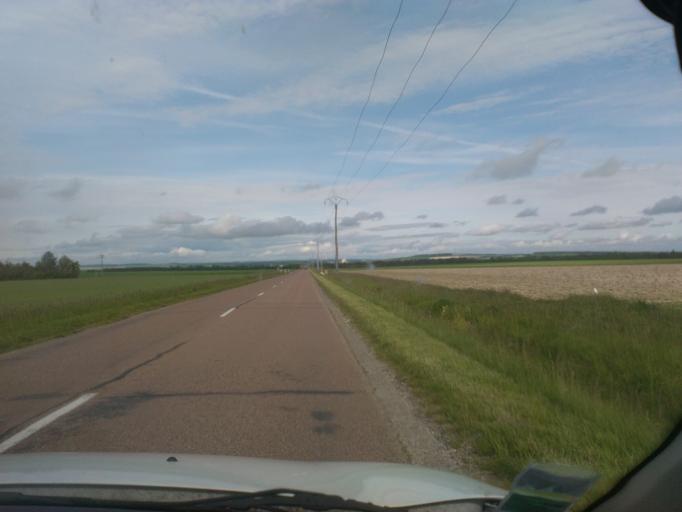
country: FR
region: Champagne-Ardenne
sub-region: Departement de l'Aube
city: Marigny-le-Chatel
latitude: 48.3933
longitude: 3.8175
